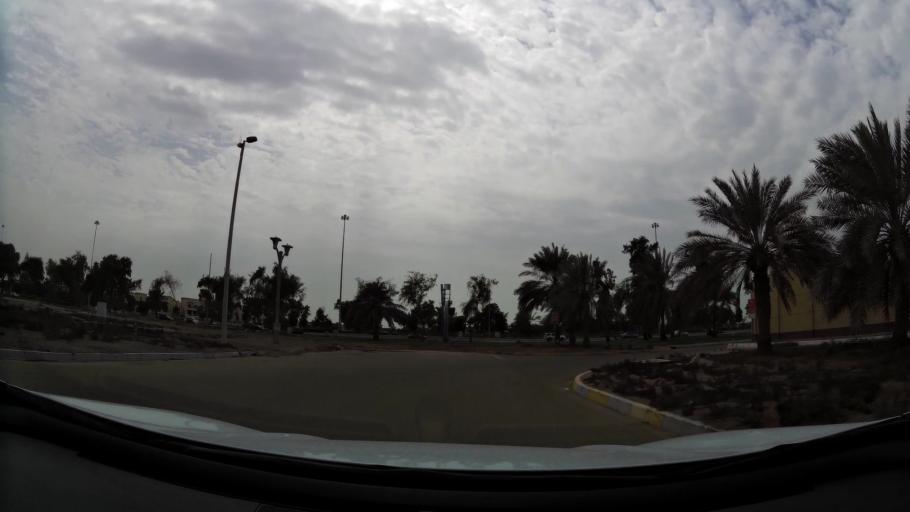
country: AE
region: Abu Dhabi
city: Abu Dhabi
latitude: 24.4099
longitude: 54.4667
